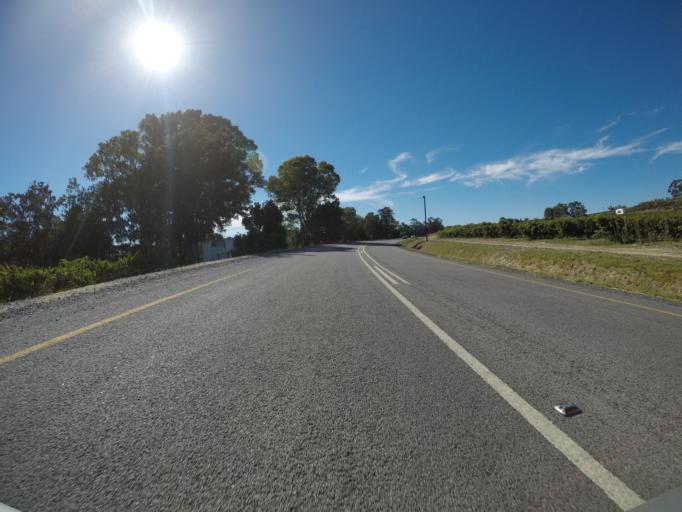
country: ZA
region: Western Cape
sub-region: Cape Winelands District Municipality
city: Stellenbosch
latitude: -33.9878
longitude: 18.7565
